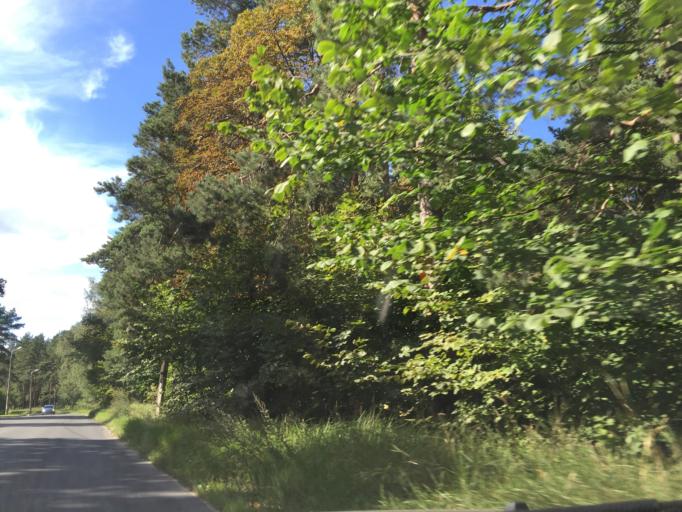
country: LV
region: Stopini
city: Ulbroka
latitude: 56.9750
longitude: 24.2317
